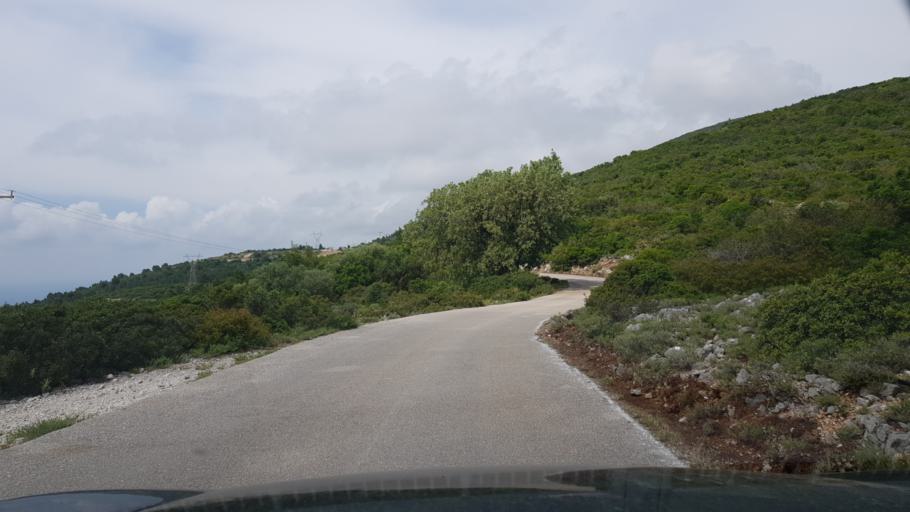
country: GR
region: Ionian Islands
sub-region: Lefkada
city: Nidri
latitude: 38.6112
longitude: 20.5645
